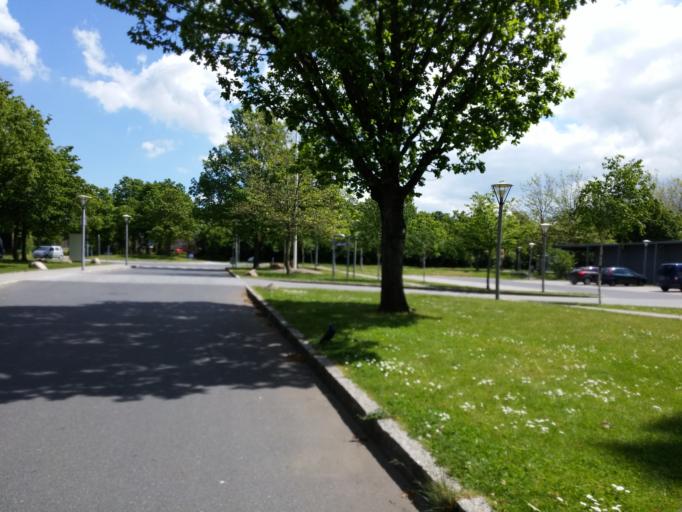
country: DK
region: South Denmark
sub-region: Odense Kommune
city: Seden
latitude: 55.4159
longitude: 10.4373
